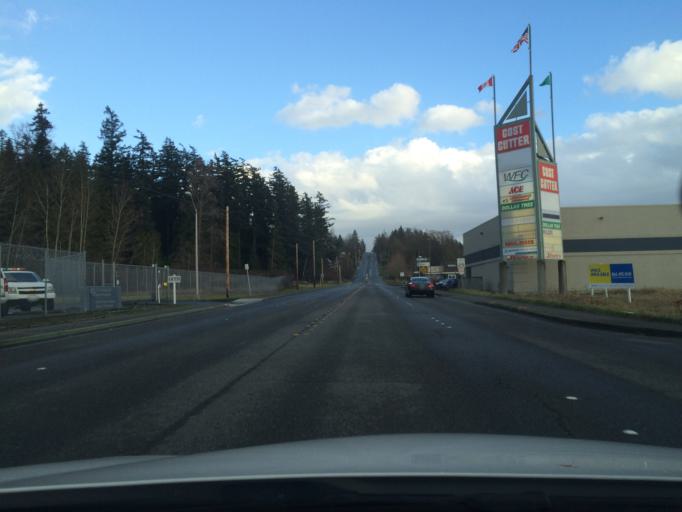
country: US
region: Washington
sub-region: Whatcom County
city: Blaine
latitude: 48.9940
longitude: -122.7315
